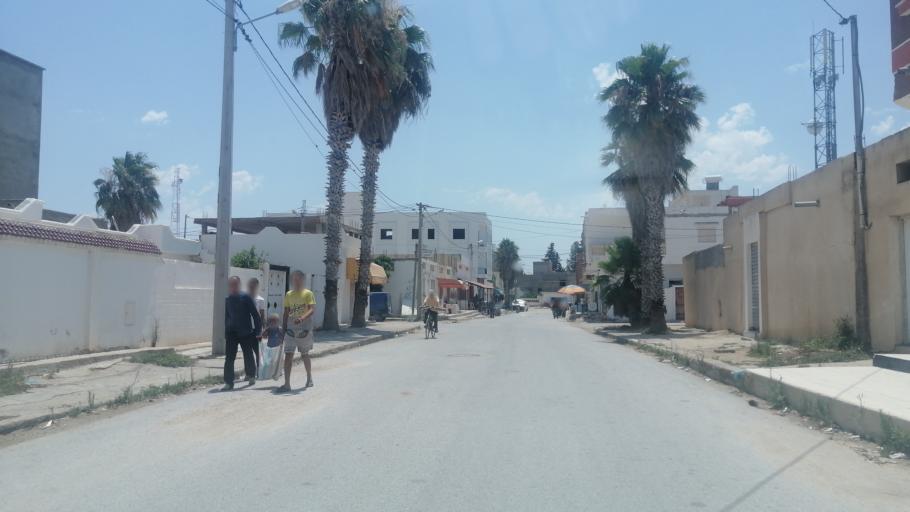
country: TN
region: Al Qayrawan
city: Sbikha
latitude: 36.1207
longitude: 10.0934
